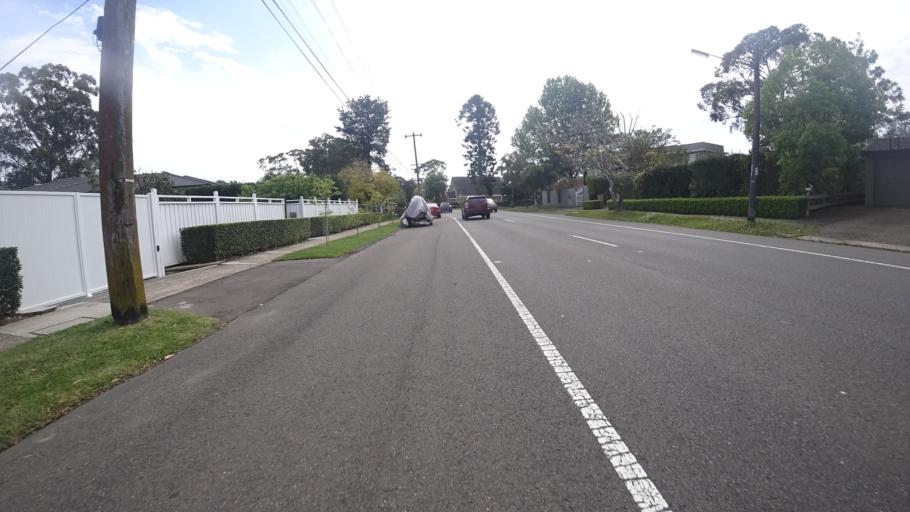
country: AU
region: New South Wales
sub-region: City of Sydney
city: North Turramurra
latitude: -33.7170
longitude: 151.1457
